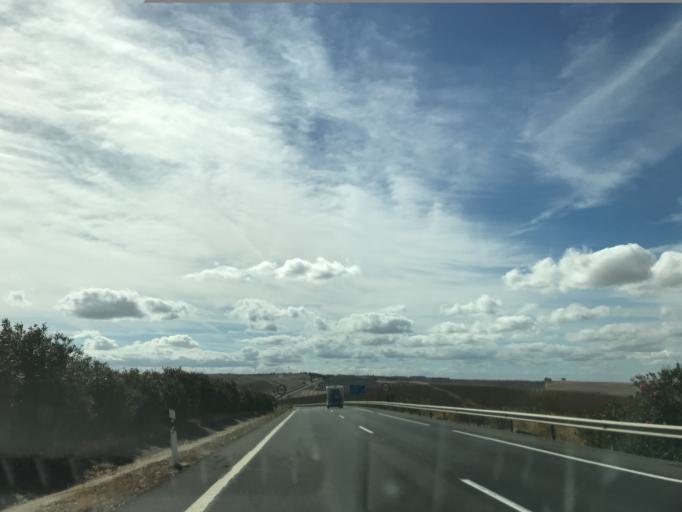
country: ES
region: Andalusia
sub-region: Province of Cordoba
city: La Victoria
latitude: 37.7447
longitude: -4.8485
